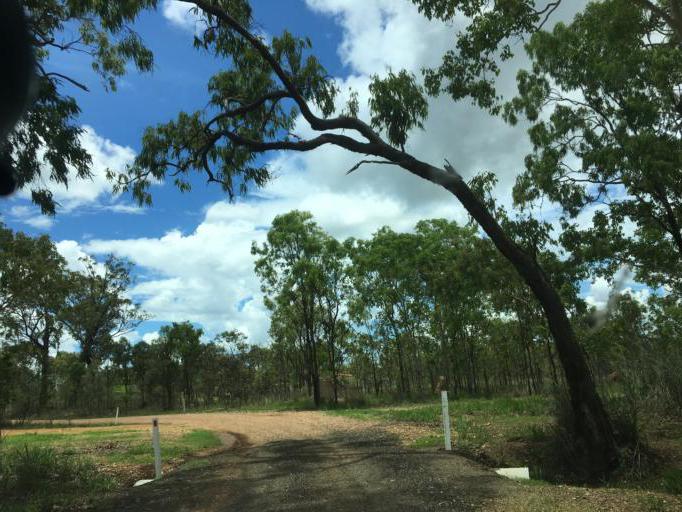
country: AU
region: Queensland
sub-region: Tablelands
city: Mareeba
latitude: -16.9929
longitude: 145.5209
